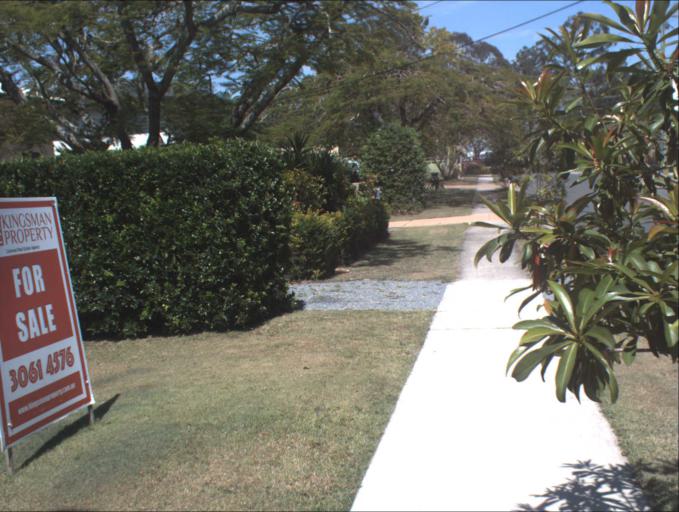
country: AU
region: Queensland
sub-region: Logan
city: Slacks Creek
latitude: -27.6306
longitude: 153.1529
